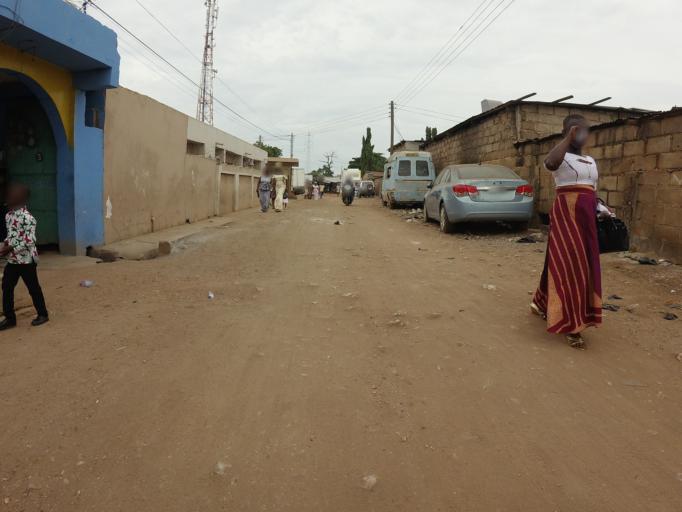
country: GH
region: Greater Accra
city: Accra
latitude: 5.5895
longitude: -0.2165
